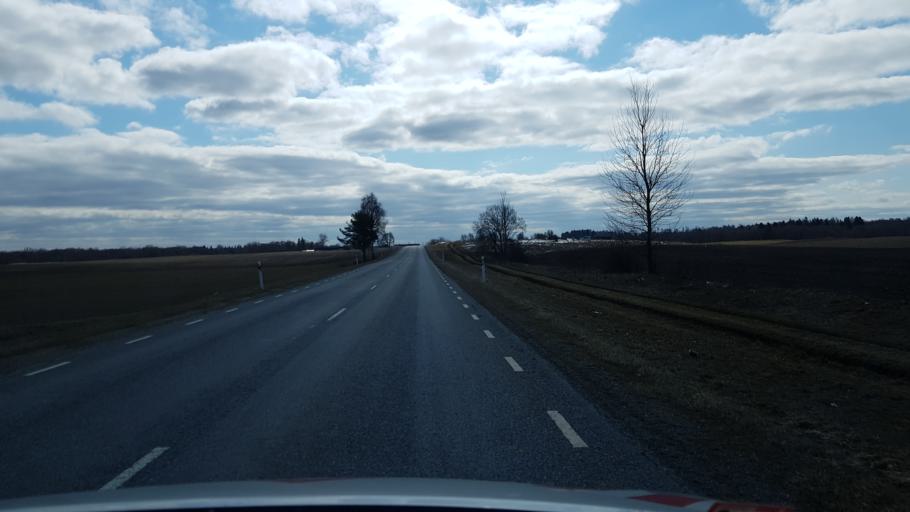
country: EE
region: Laeaene-Virumaa
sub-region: Tapa vald
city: Tapa
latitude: 59.3337
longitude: 25.9999
